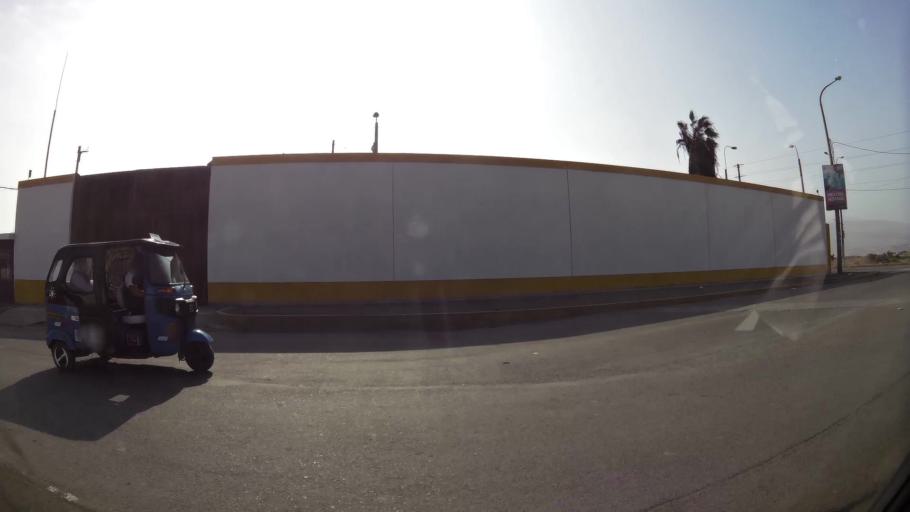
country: PE
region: Lima
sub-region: Lima
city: Santa Rosa
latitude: -11.7737
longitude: -77.1679
